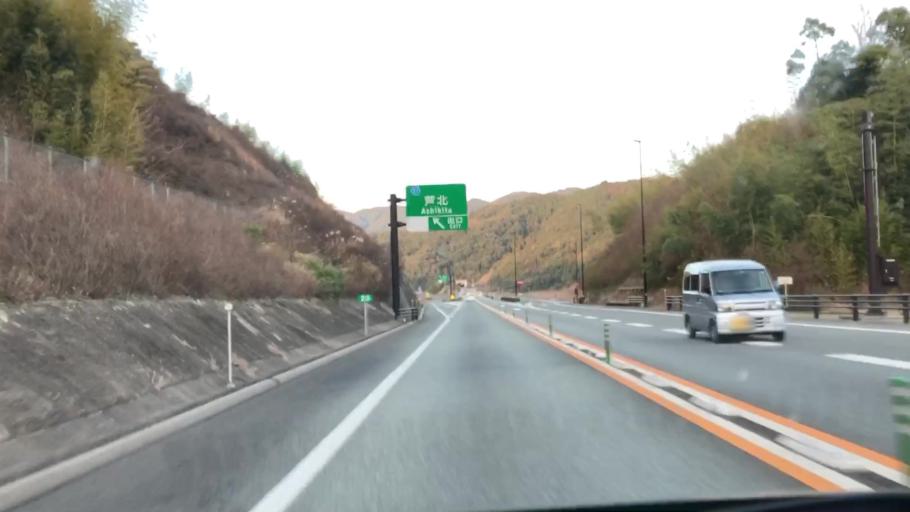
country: JP
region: Kumamoto
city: Minamata
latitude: 32.2951
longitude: 130.5078
